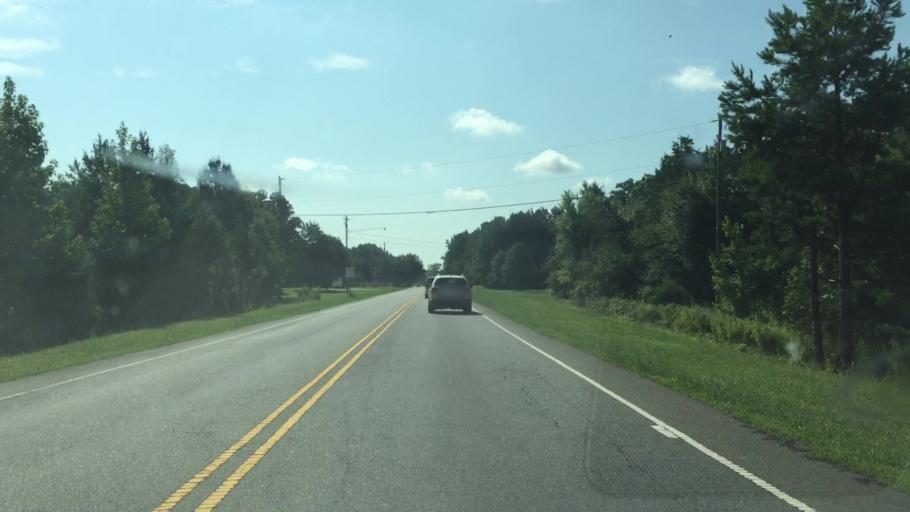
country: US
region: North Carolina
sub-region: Mecklenburg County
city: Mint Hill
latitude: 35.1755
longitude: -80.6230
